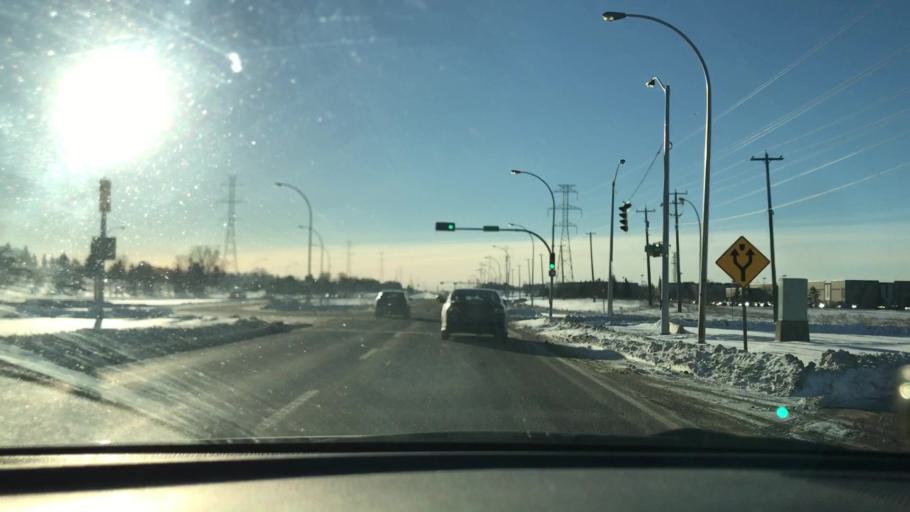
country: CA
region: Alberta
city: Edmonton
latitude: 53.4592
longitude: -113.4669
